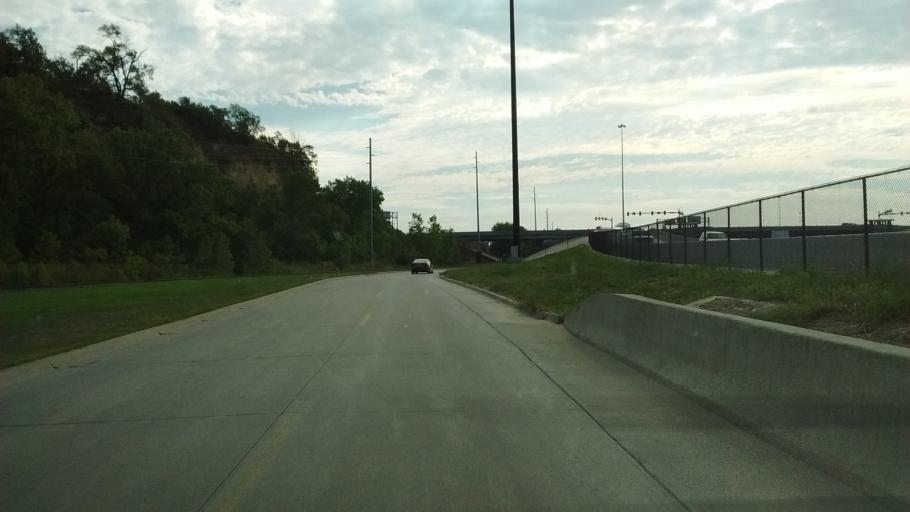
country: US
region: Iowa
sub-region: Woodbury County
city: Sioux City
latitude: 42.4925
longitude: -96.4160
